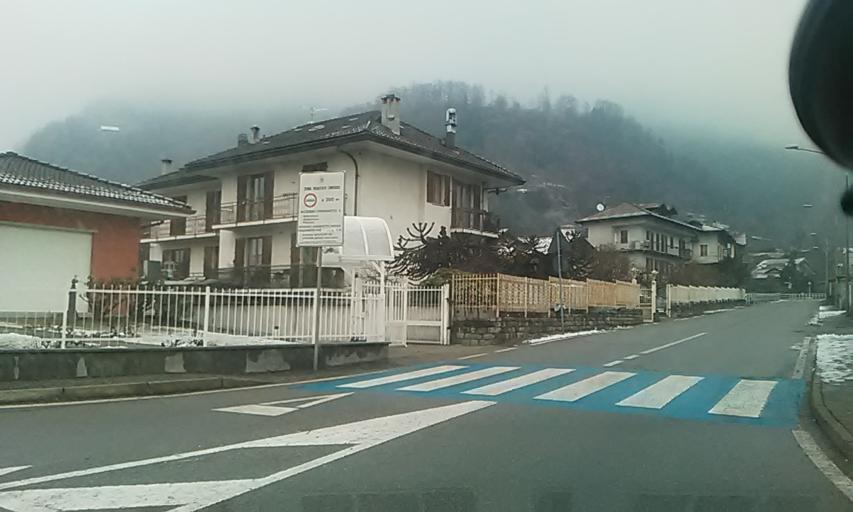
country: IT
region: Piedmont
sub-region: Provincia di Vercelli
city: Varallo
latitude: 45.8134
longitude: 8.2655
